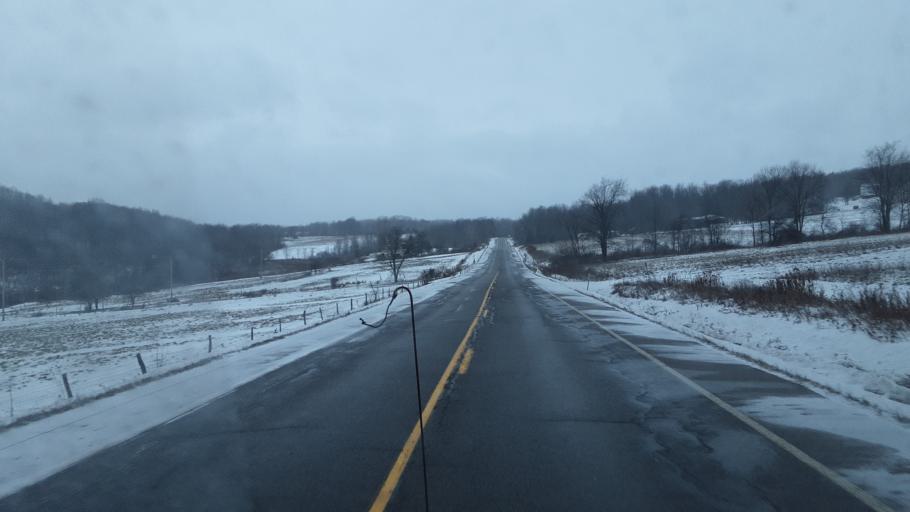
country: US
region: Pennsylvania
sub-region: Tioga County
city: Westfield
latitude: 42.0929
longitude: -77.5389
